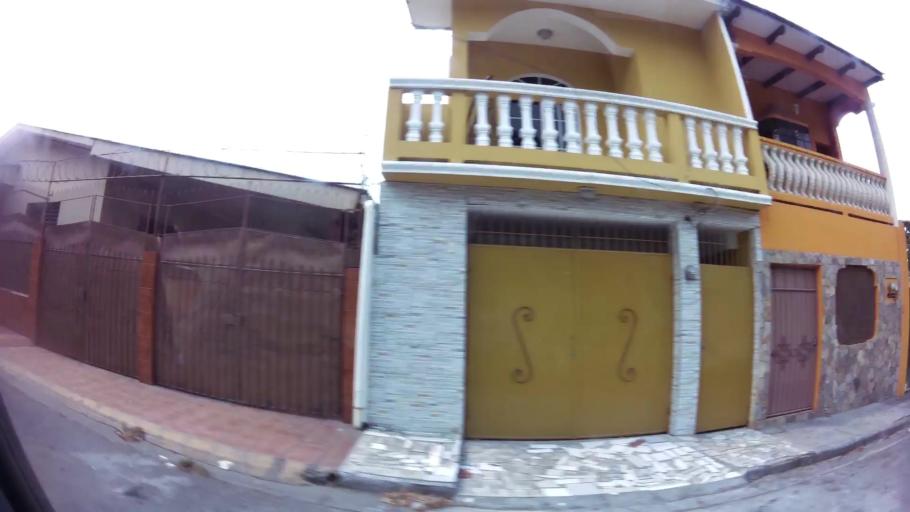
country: HN
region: Cortes
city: San Pedro Sula
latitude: 15.4920
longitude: -88.0310
